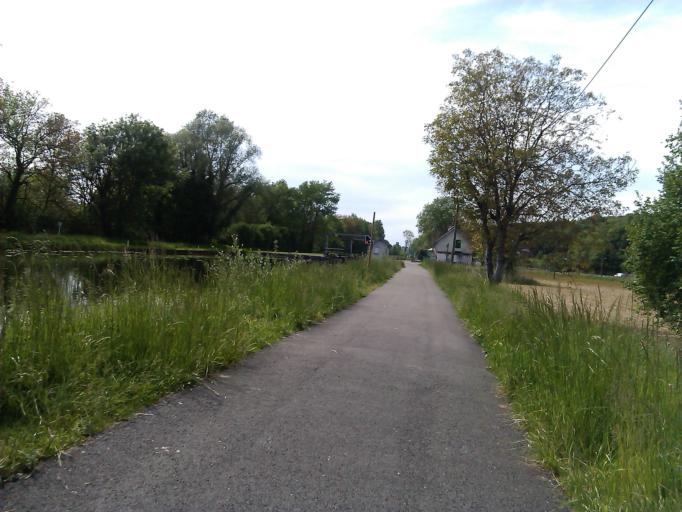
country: FR
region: Franche-Comte
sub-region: Departement du Doubs
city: Saint-Vit
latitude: 47.1663
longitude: 5.8438
